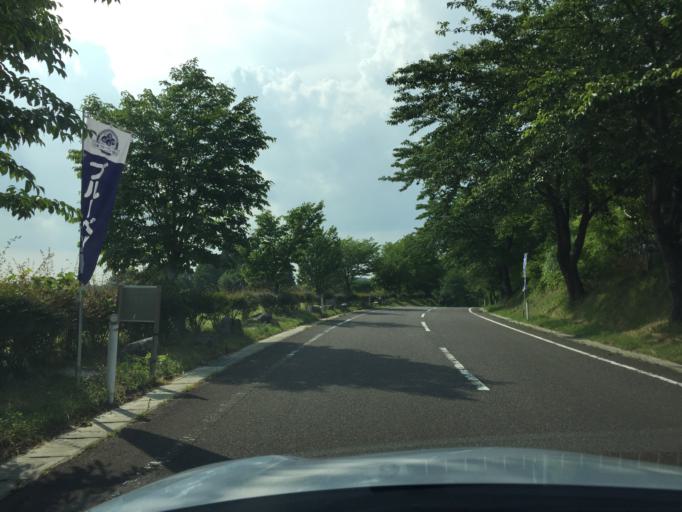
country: JP
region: Fukushima
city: Miharu
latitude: 37.4090
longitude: 140.4951
